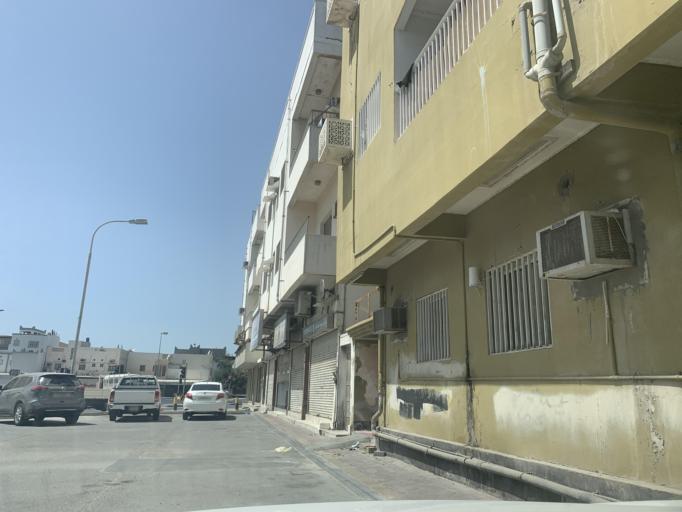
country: BH
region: Northern
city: Sitrah
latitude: 26.1645
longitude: 50.6084
